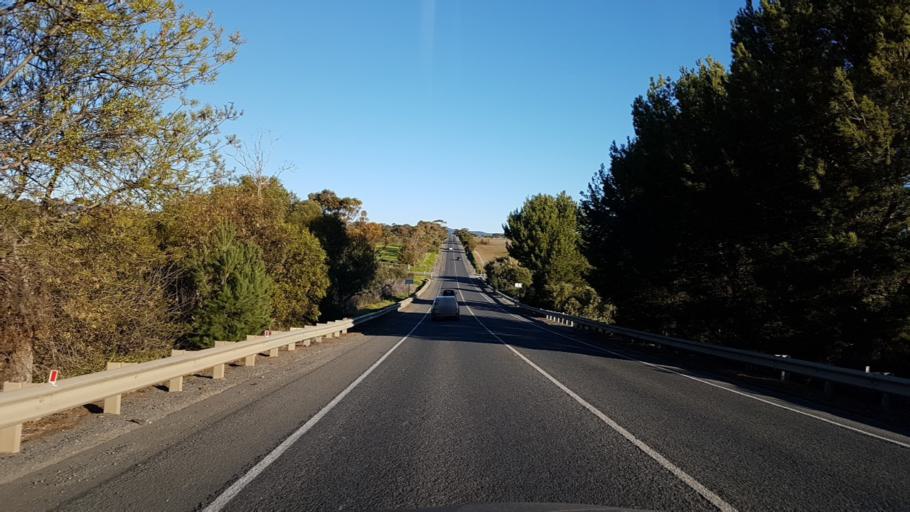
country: AU
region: South Australia
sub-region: Onkaparinga
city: Aldinga
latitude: -35.2423
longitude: 138.4941
